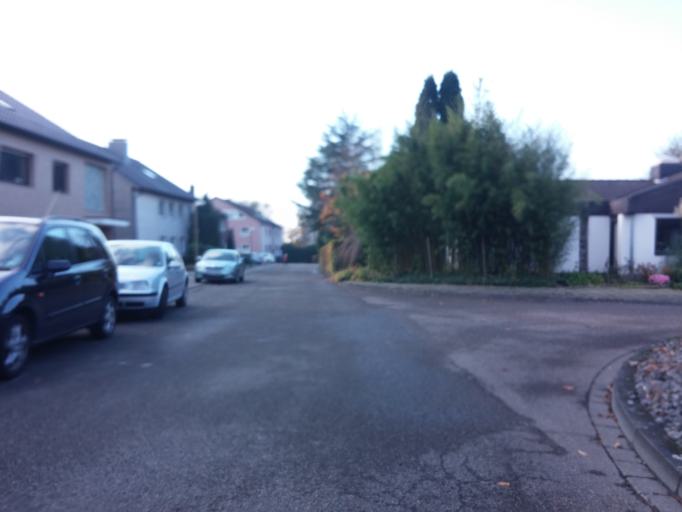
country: DE
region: North Rhine-Westphalia
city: Marl
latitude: 51.6466
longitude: 7.0953
